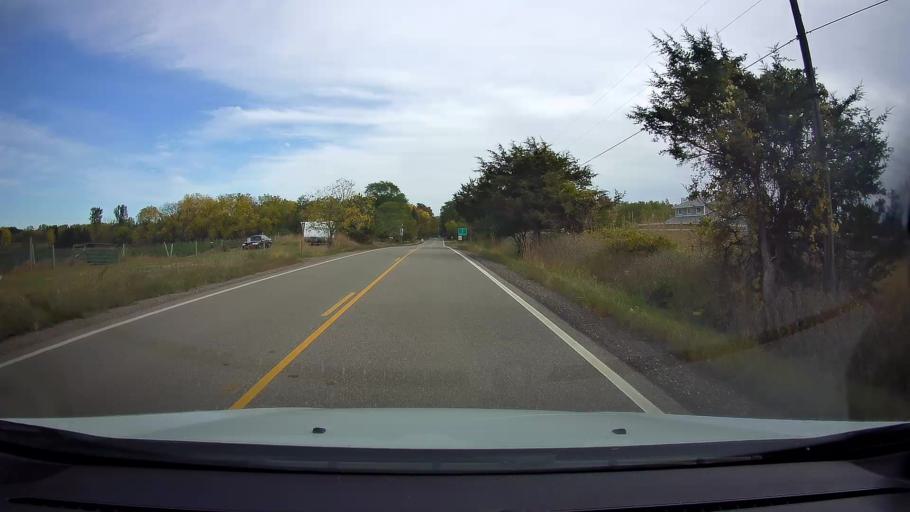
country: US
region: Minnesota
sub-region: Washington County
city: Stillwater
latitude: 45.0982
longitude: -92.8163
